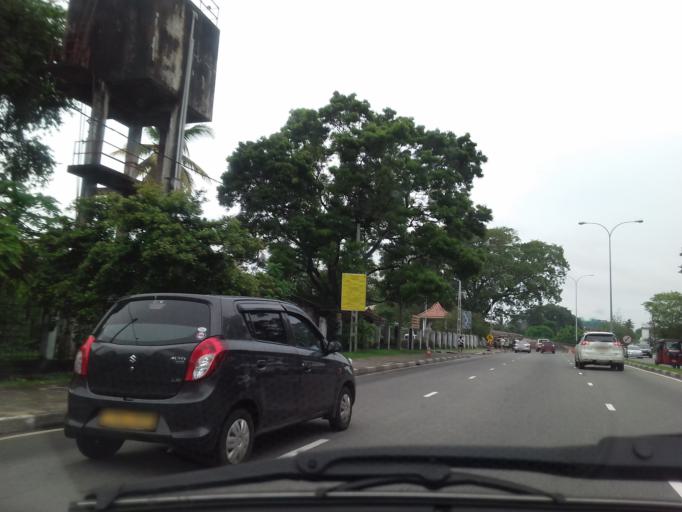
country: LK
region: Western
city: Pita Kotte
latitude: 6.9085
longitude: 79.8928
